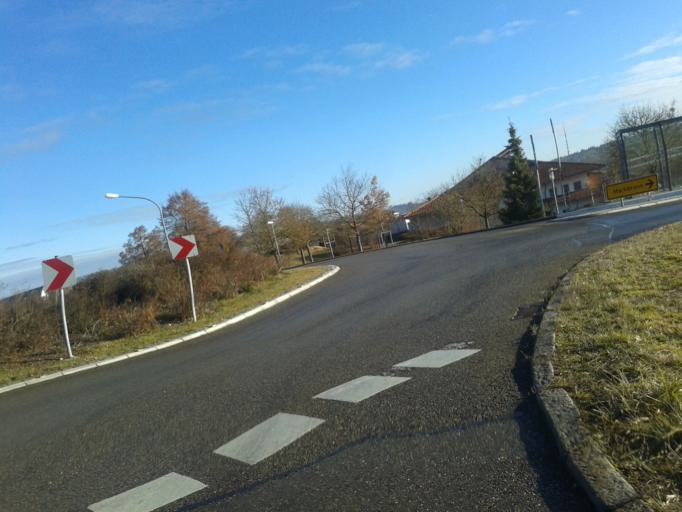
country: DE
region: Baden-Wuerttemberg
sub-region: Tuebingen Region
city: Erbach
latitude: 48.3930
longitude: 9.8599
